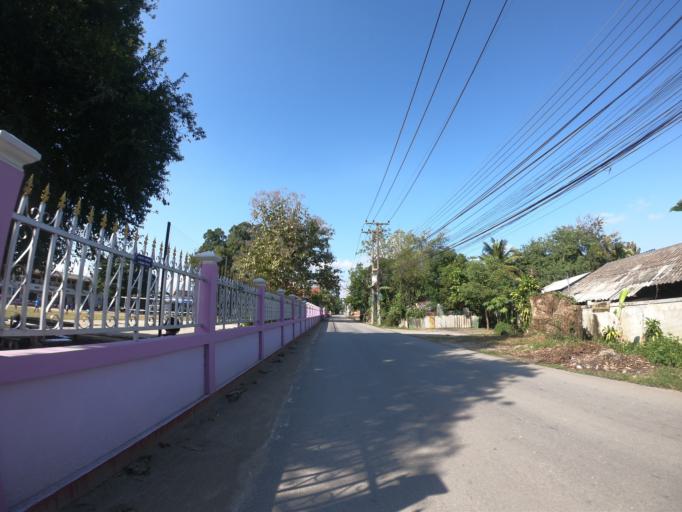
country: TH
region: Chiang Mai
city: Saraphi
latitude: 18.7162
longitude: 99.0038
